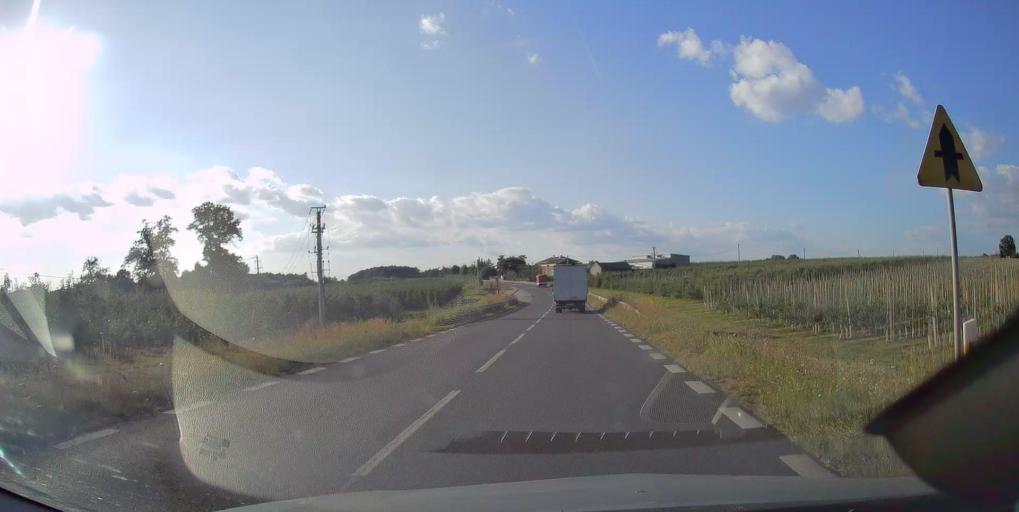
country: PL
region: Lodz Voivodeship
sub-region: Powiat rawski
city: Biala Rawska
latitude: 51.8042
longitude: 20.5031
